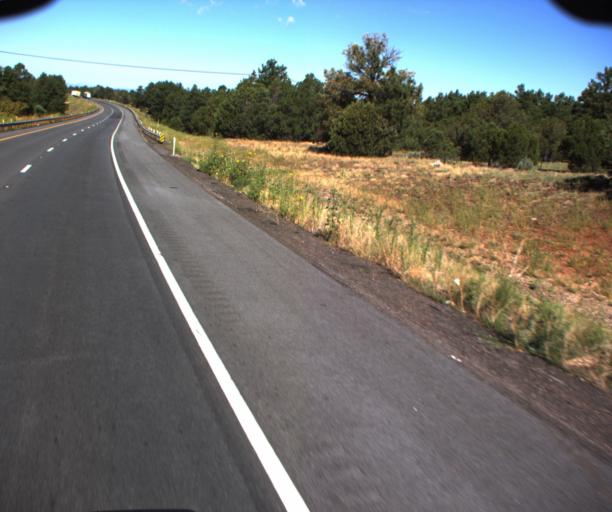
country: US
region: Arizona
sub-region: Coconino County
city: Williams
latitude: 35.2241
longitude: -112.2456
